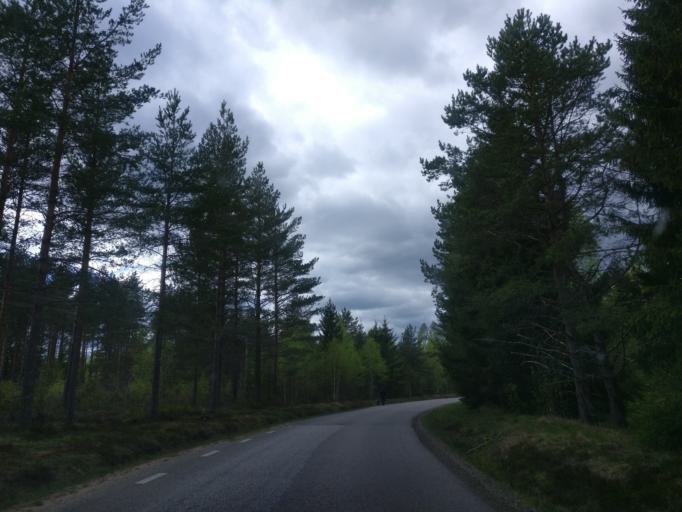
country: SE
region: Gaevleborg
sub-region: Hudiksvalls Kommun
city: Iggesund
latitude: 61.5031
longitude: 17.0199
